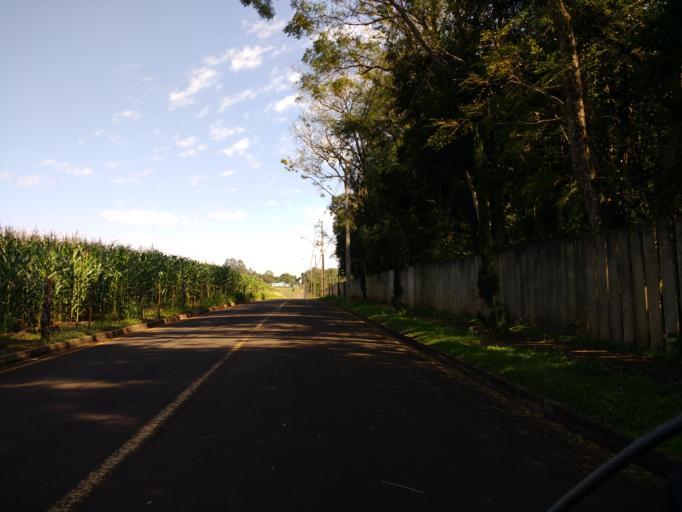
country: BR
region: Parana
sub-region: Londrina
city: Londrina
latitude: -23.3668
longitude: -51.1898
